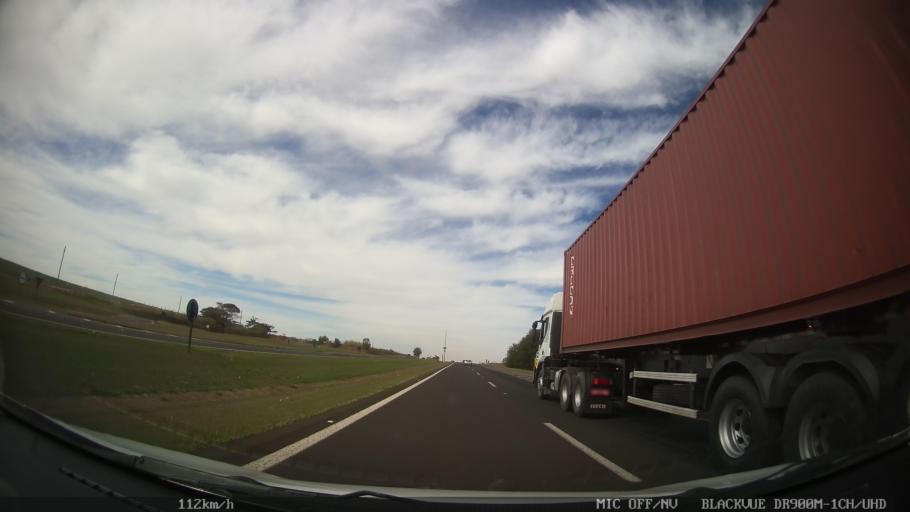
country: BR
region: Sao Paulo
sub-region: Matao
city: Matao
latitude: -21.5574
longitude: -48.4801
